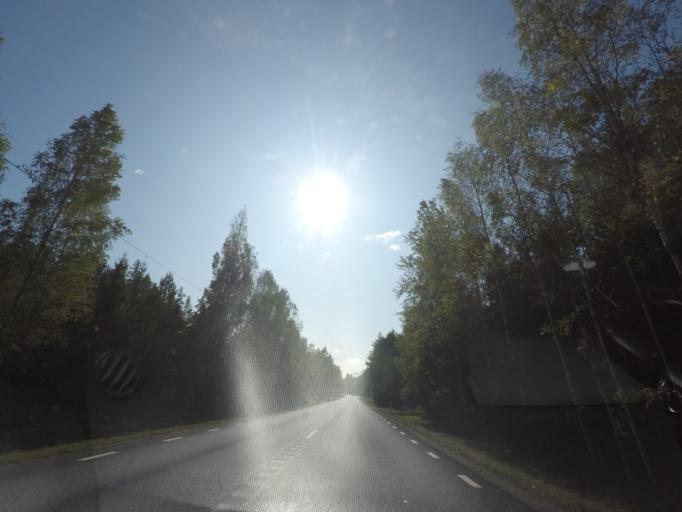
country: SE
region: Vaestmanland
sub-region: Skinnskattebergs Kommun
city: Skinnskatteberg
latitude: 59.8175
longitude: 15.5305
